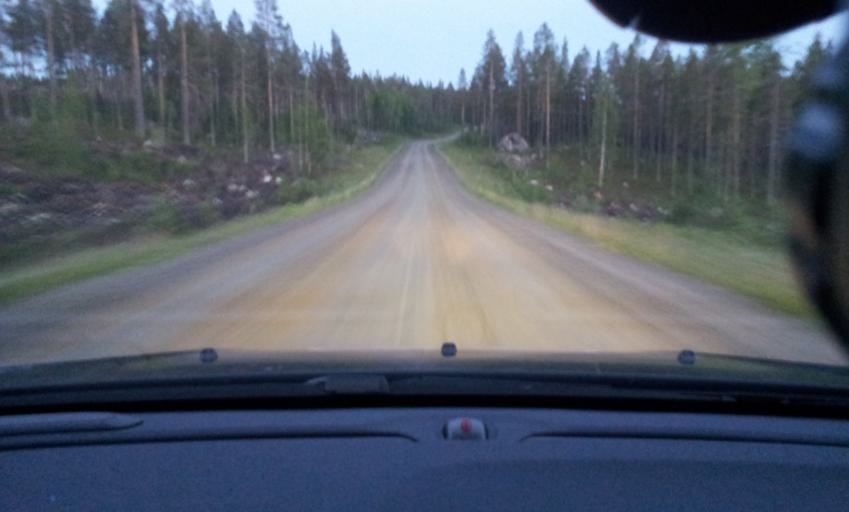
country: SE
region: Vaesternorrland
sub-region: Ange Kommun
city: Ange
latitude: 62.7374
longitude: 15.6432
